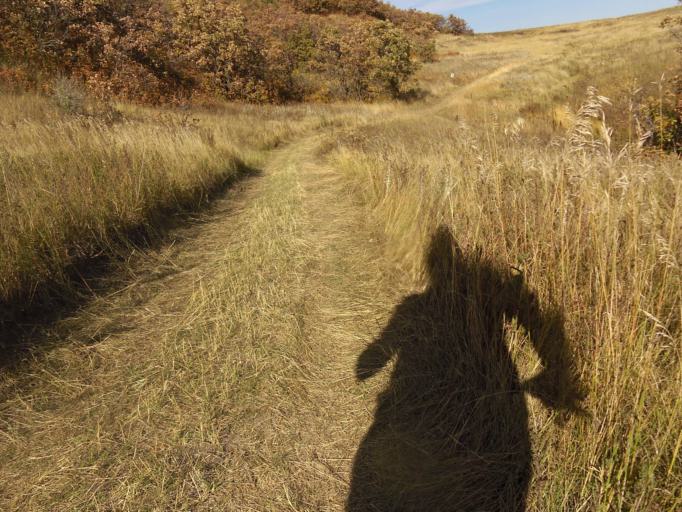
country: CA
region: Manitoba
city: Morden
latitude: 48.9483
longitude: -98.0662
